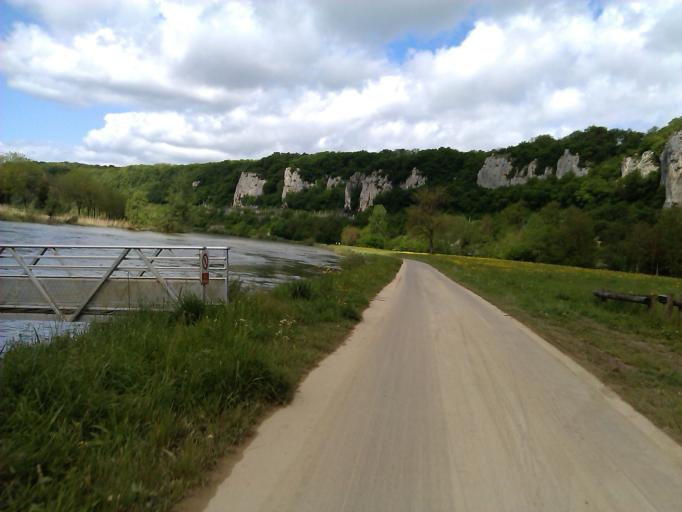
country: FR
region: Franche-Comte
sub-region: Departement du Doubs
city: Baume-les-Dames
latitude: 47.3299
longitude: 6.3020
